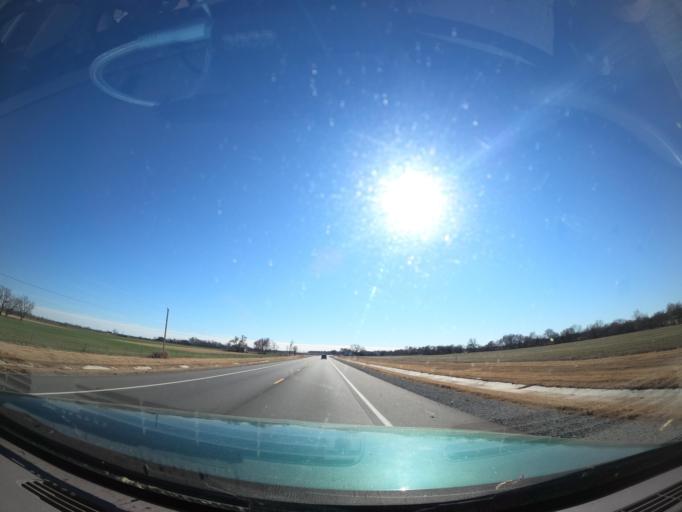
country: US
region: Oklahoma
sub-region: Wagoner County
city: Coweta
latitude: 35.8920
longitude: -95.6592
